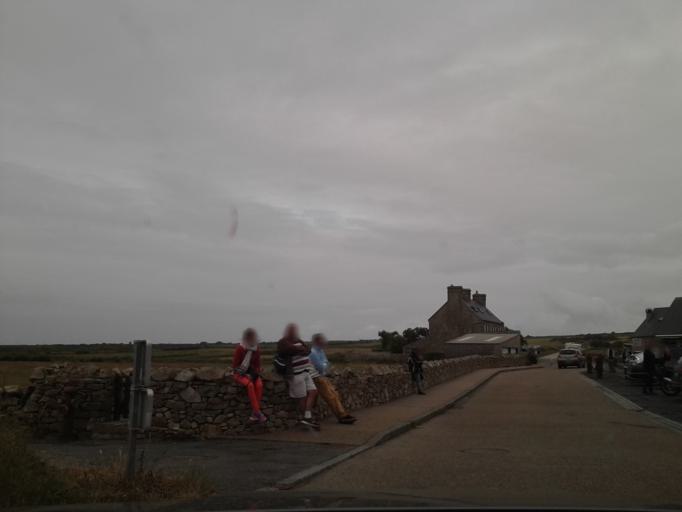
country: FR
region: Lower Normandy
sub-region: Departement de la Manche
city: Beaumont-Hague
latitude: 49.7158
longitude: -1.9457
